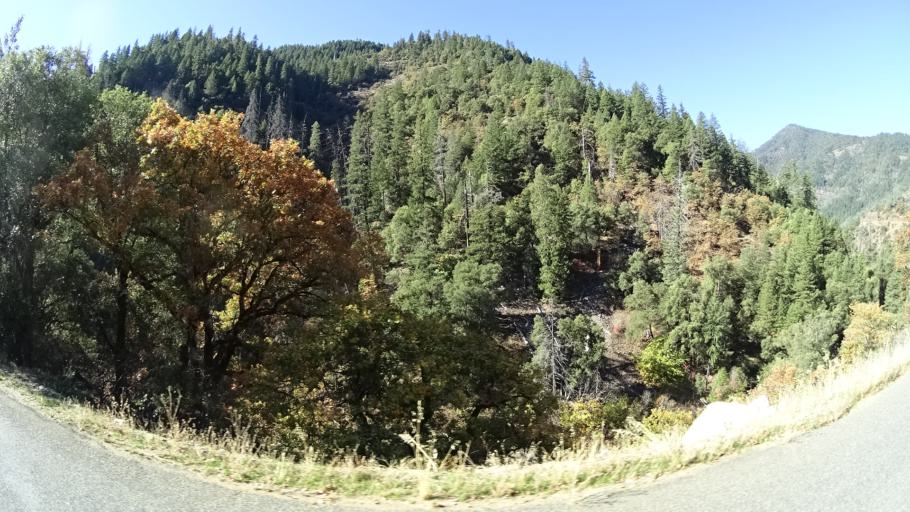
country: US
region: California
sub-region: Humboldt County
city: Willow Creek
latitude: 41.1460
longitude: -123.2007
